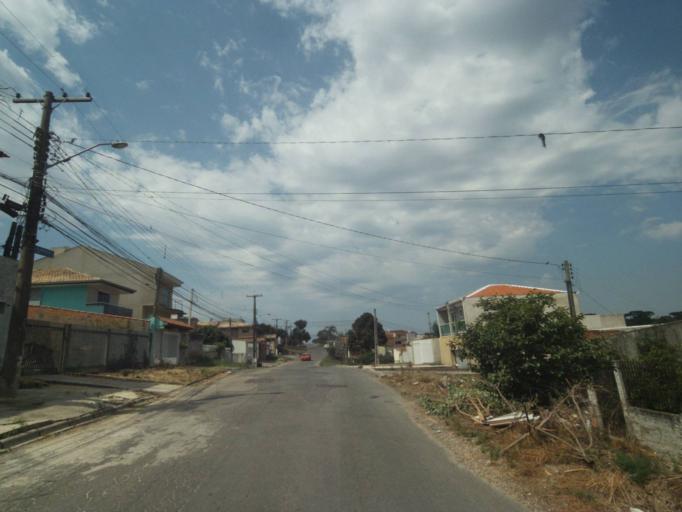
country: BR
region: Parana
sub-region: Sao Jose Dos Pinhais
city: Sao Jose dos Pinhais
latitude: -25.5262
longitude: -49.2595
